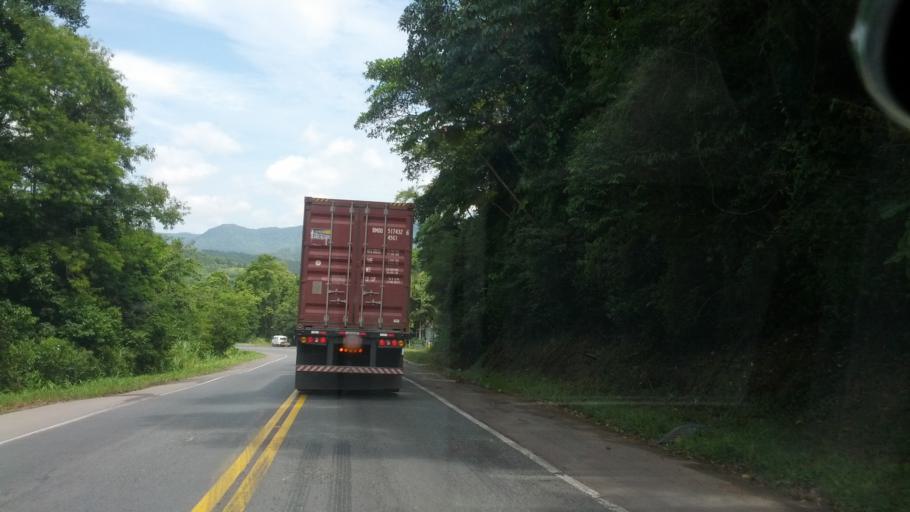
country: BR
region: Santa Catarina
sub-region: Ibirama
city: Ibirama
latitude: -27.0800
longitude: -49.5180
